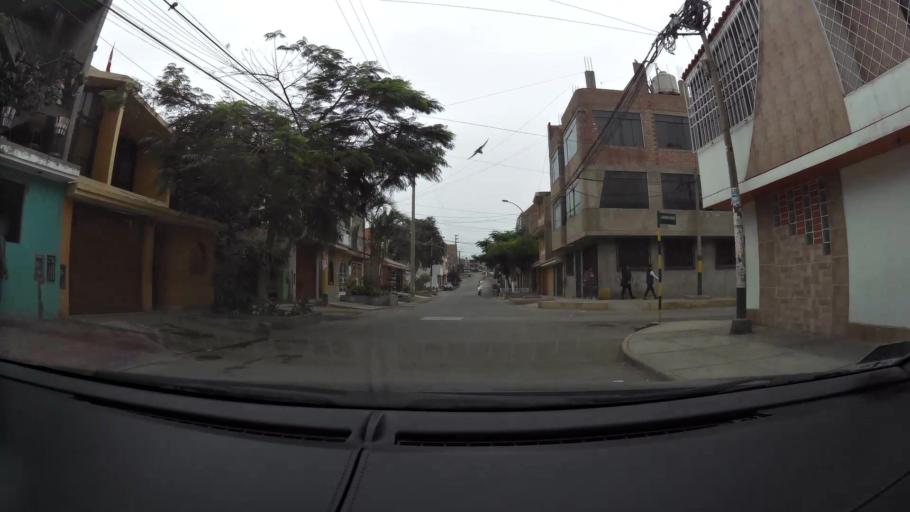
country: PE
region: Lima
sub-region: Lima
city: Independencia
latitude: -11.9481
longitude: -77.0912
